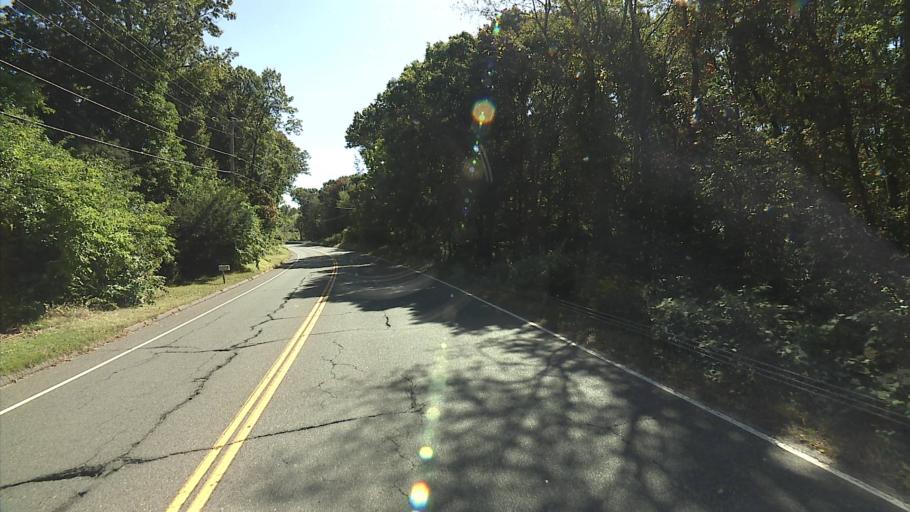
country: US
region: Connecticut
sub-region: New Haven County
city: Prospect
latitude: 41.5267
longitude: -73.0018
